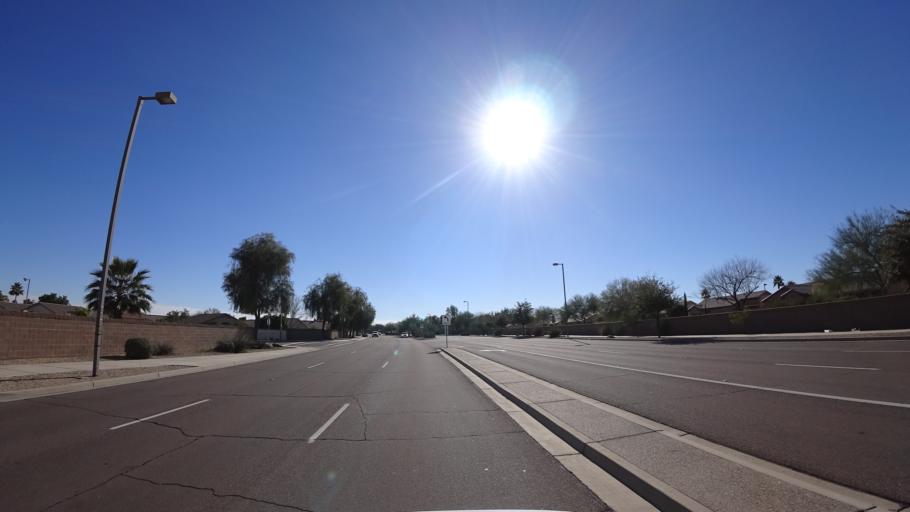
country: US
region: Arizona
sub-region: Maricopa County
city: Sun City West
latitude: 33.6425
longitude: -112.3933
